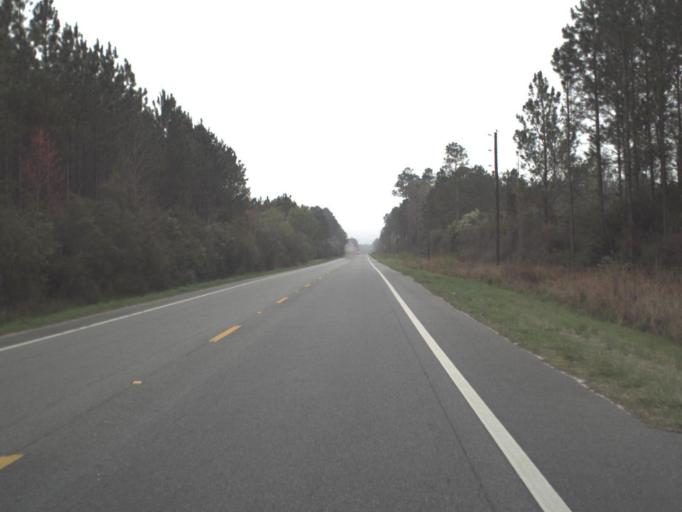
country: US
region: Florida
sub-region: Liberty County
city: Bristol
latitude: 30.3467
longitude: -84.8203
